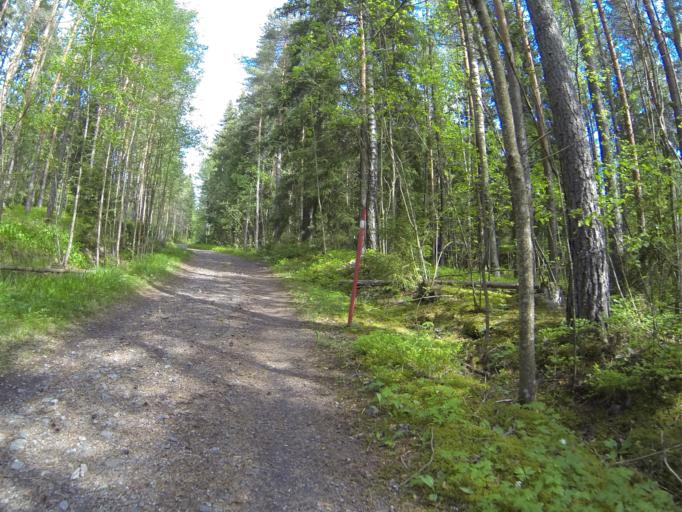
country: FI
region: Varsinais-Suomi
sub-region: Salo
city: Salo
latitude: 60.3863
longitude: 23.1733
